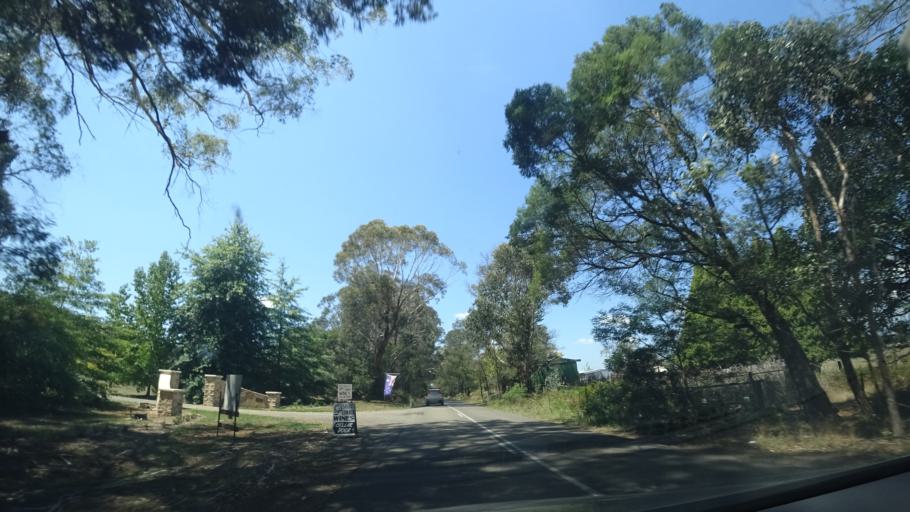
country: AU
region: New South Wales
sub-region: Wingecarribee
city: Bundanoon
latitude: -34.6113
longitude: 150.2558
